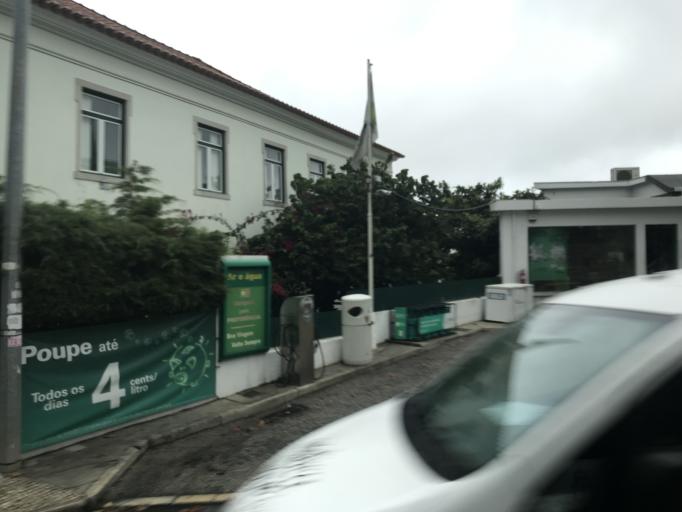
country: PT
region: Lisbon
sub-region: Sintra
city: Sintra
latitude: 38.7997
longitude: -9.3821
